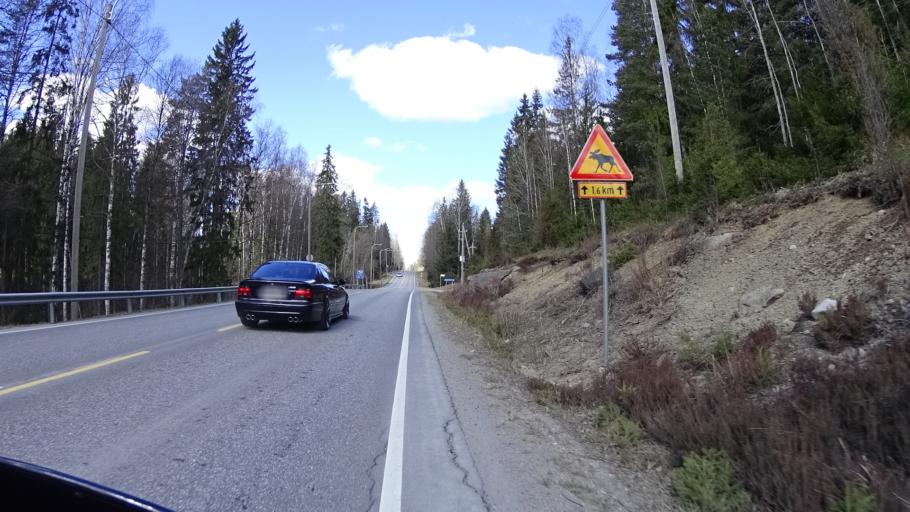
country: FI
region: Uusimaa
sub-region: Helsinki
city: Kirkkonummi
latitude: 60.2536
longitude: 24.5073
